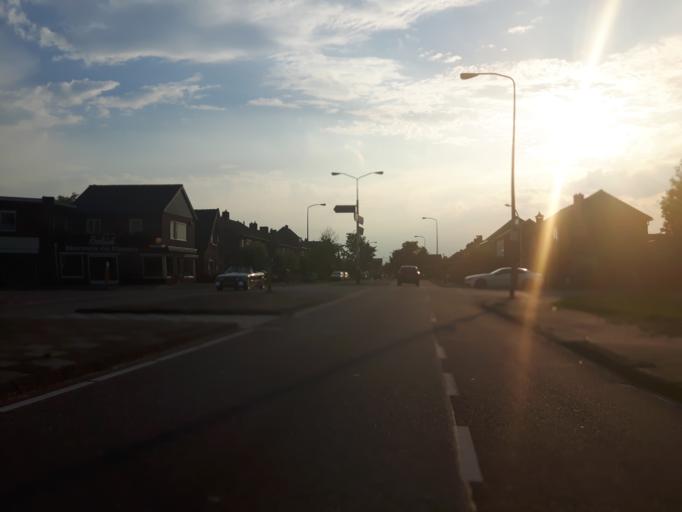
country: NL
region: Overijssel
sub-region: Gemeente Hengelo
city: Hengelo
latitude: 52.2510
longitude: 6.8012
